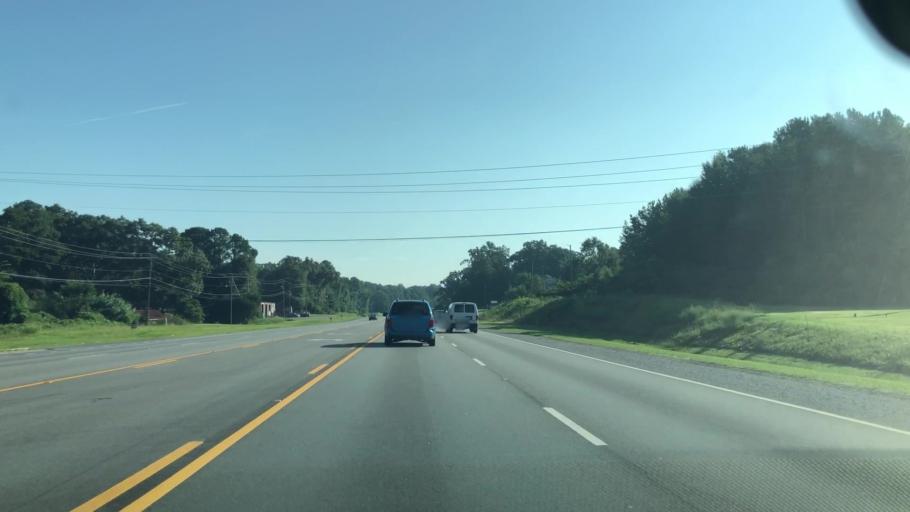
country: US
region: Alabama
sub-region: Calhoun County
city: Bynum
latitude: 33.6270
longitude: -85.9181
